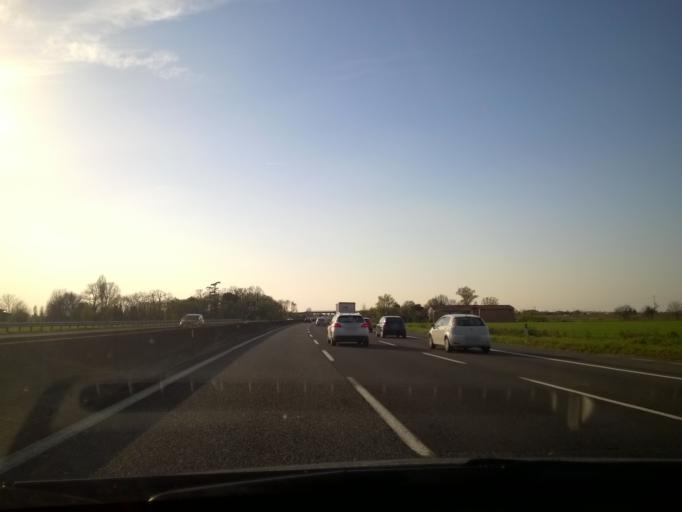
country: IT
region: Emilia-Romagna
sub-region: Provincia di Bologna
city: Imola
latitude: 44.3929
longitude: 11.7084
